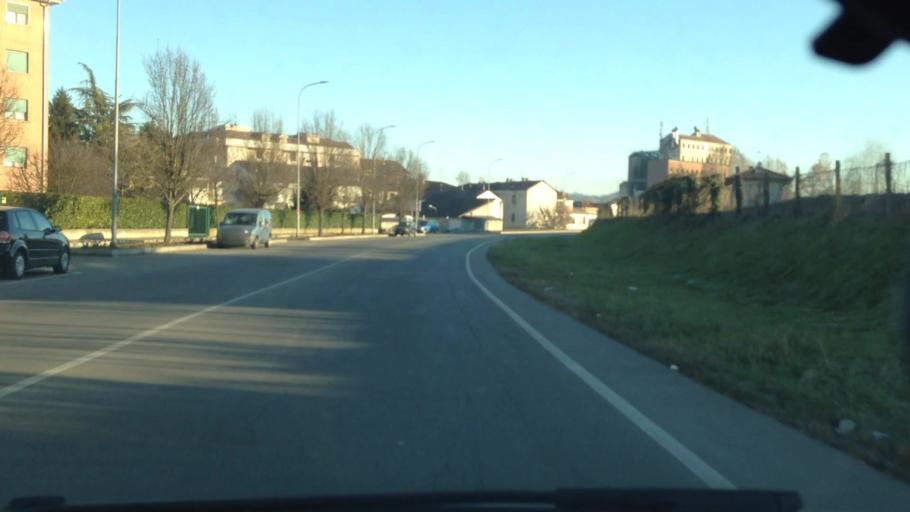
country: IT
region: Piedmont
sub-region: Provincia di Asti
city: Asti
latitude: 44.8884
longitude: 8.2093
